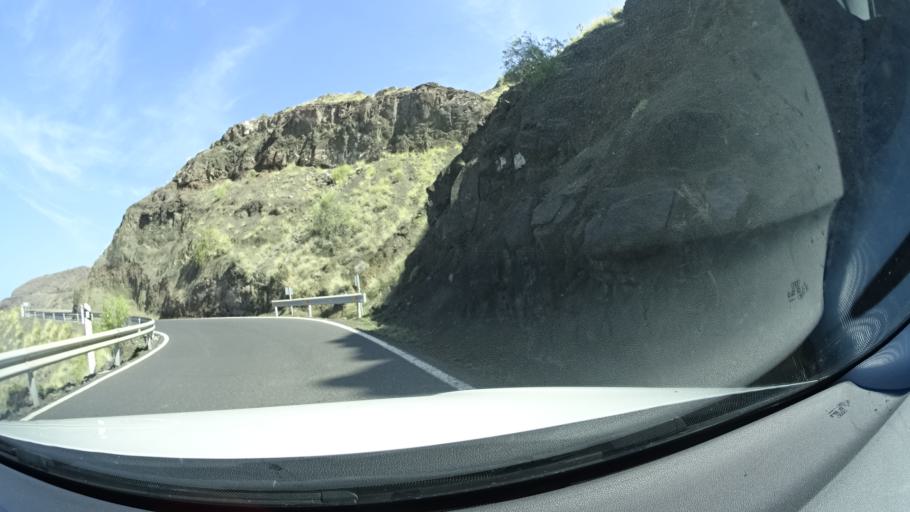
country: ES
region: Canary Islands
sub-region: Provincia de Las Palmas
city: Agaete
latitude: 28.0862
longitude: -15.7046
